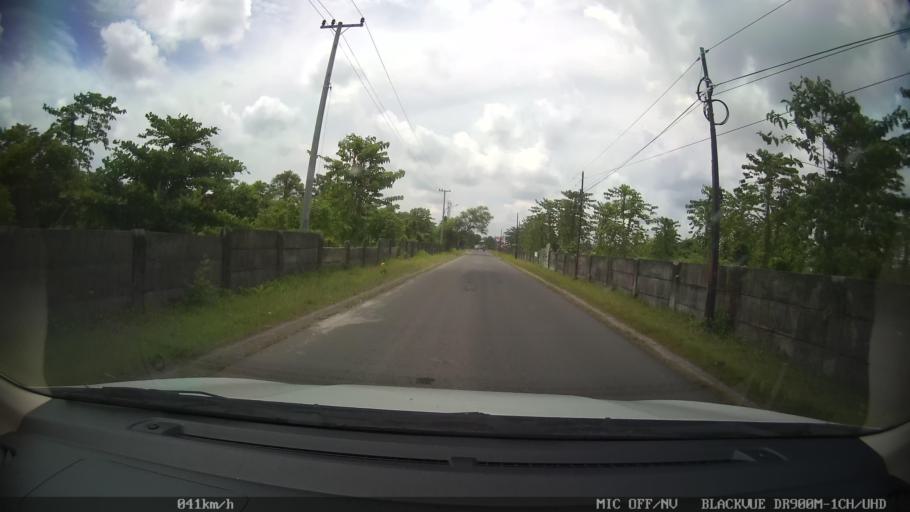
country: ID
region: North Sumatra
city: Medan
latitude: 3.6013
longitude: 98.7286
